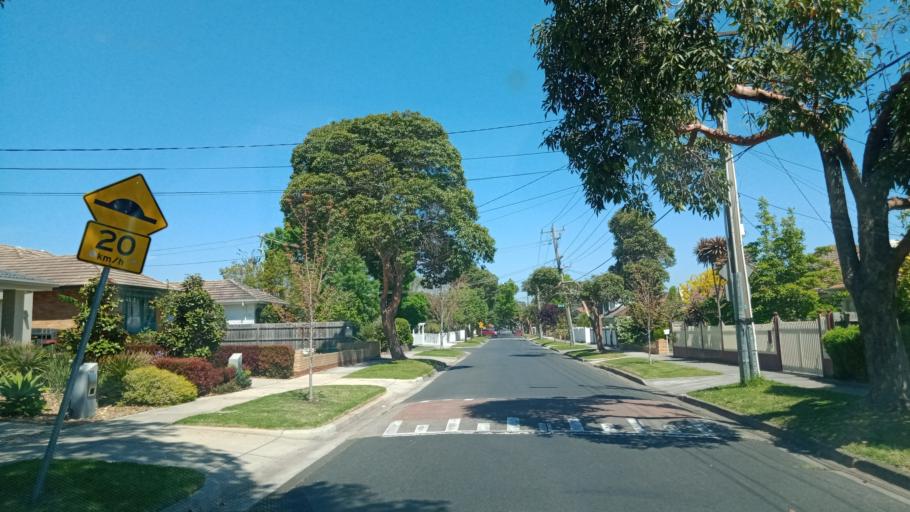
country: AU
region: Victoria
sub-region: Monash
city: Oakleigh South
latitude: -37.9247
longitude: 145.0793
